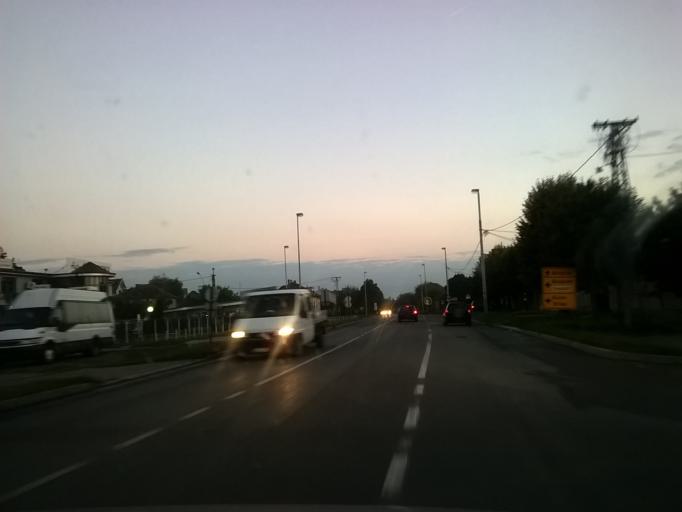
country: RS
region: Autonomna Pokrajina Vojvodina
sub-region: Juznobanatski Okrug
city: Pancevo
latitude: 44.8847
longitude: 20.6310
